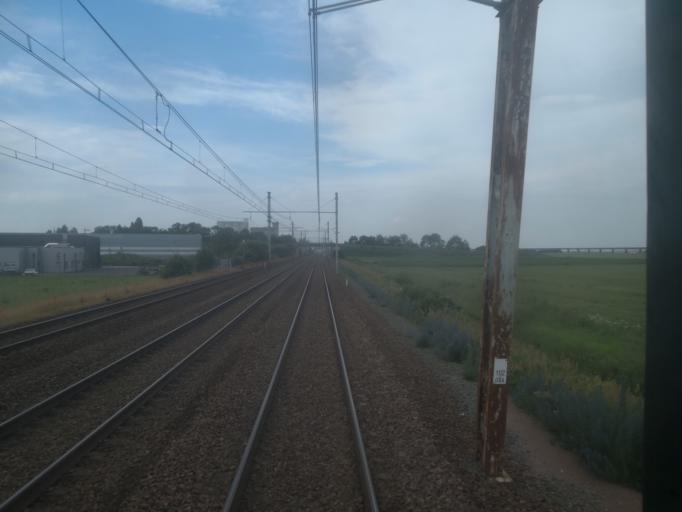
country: FR
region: Centre
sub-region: Departement du Loiret
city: Artenay
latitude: 48.0744
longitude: 1.8803
